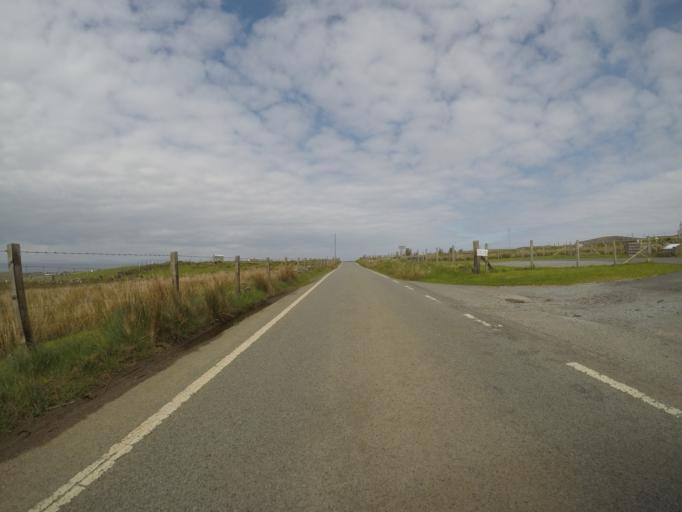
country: GB
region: Scotland
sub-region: Highland
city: Portree
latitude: 57.6405
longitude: -6.3765
